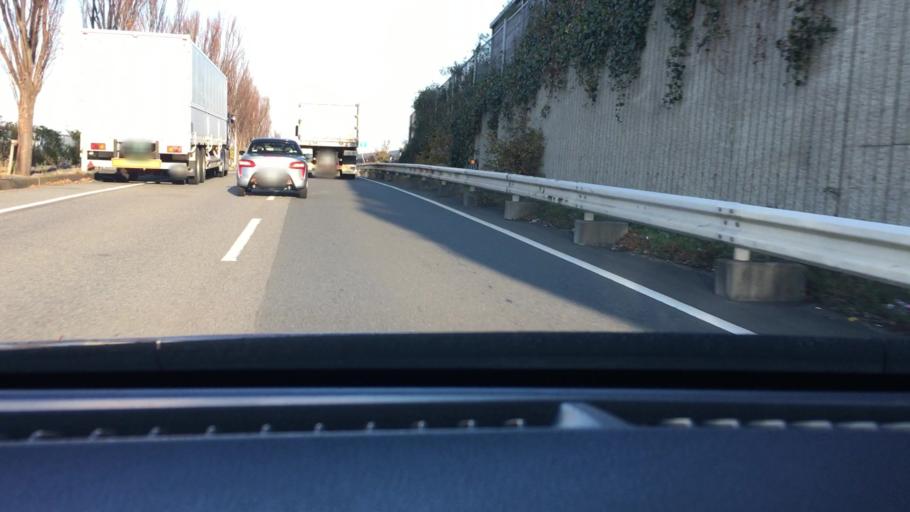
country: JP
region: Chiba
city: Kisarazu
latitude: 35.4291
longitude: 139.9268
